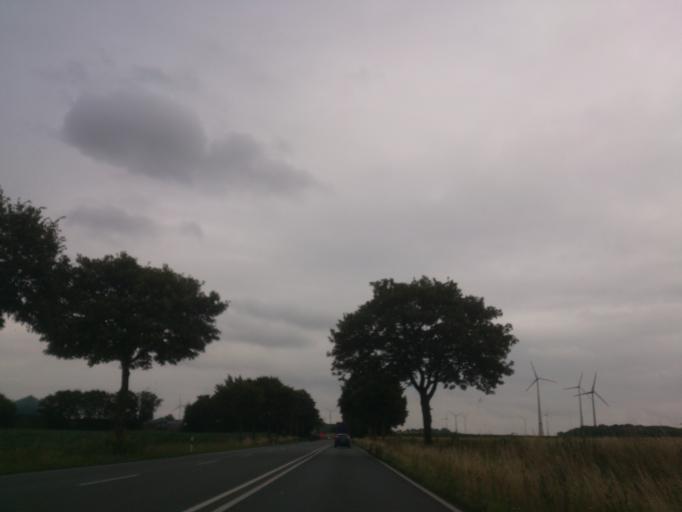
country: DE
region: North Rhine-Westphalia
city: Bad Lippspringe
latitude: 51.7212
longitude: 8.8450
